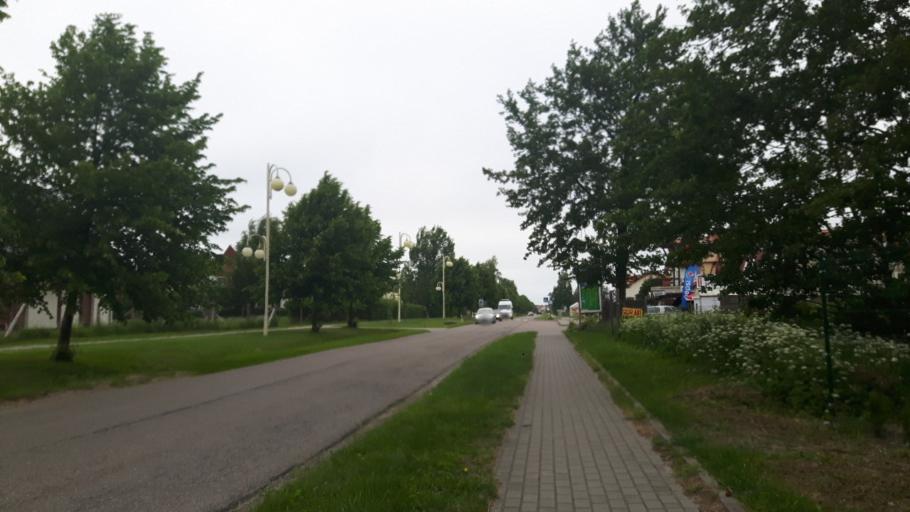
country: PL
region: Pomeranian Voivodeship
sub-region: Powiat slupski
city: Smoldzino
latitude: 54.6532
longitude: 17.0507
